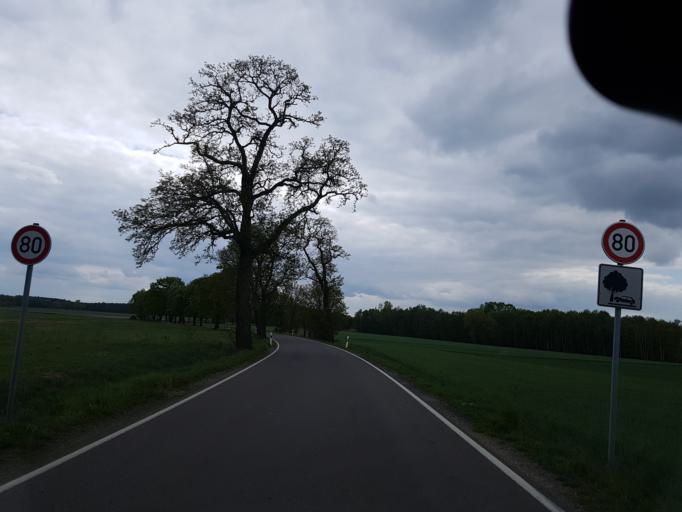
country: DE
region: Brandenburg
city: Bronkow
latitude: 51.6277
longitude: 13.9288
